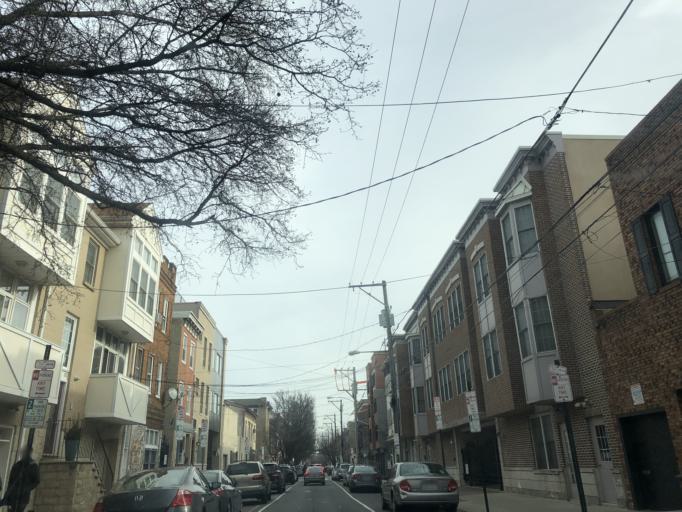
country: US
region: Pennsylvania
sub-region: Philadelphia County
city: Philadelphia
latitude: 39.9414
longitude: -75.1551
